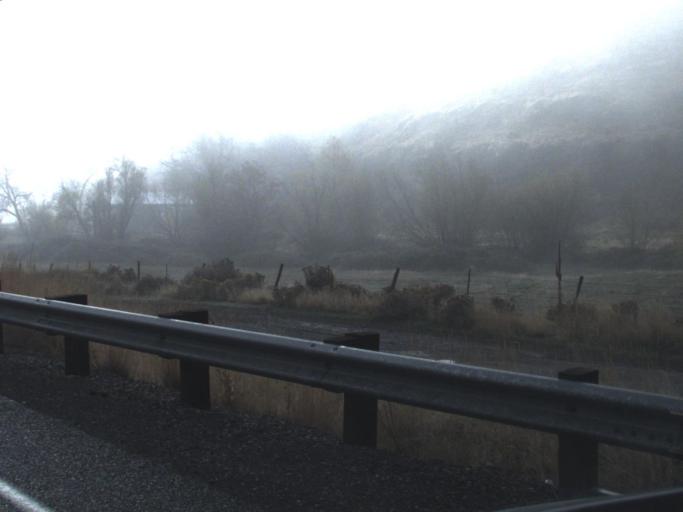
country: US
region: Washington
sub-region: Asotin County
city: Clarkston Heights-Vineland
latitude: 46.4354
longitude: -117.3218
